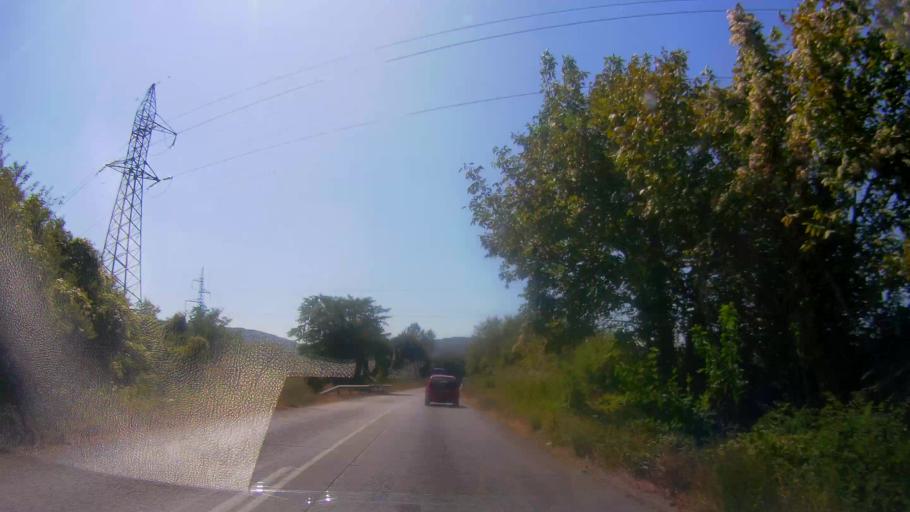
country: BG
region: Veliko Turnovo
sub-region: Obshtina Gorna Oryakhovitsa
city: Purvomaytsi
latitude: 43.1530
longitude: 25.6182
